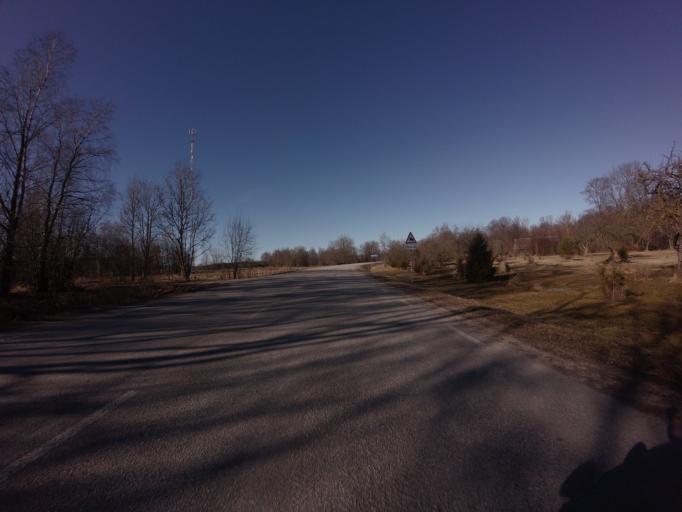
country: EE
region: Saare
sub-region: Kuressaare linn
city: Kuressaare
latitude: 58.4707
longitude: 22.2276
